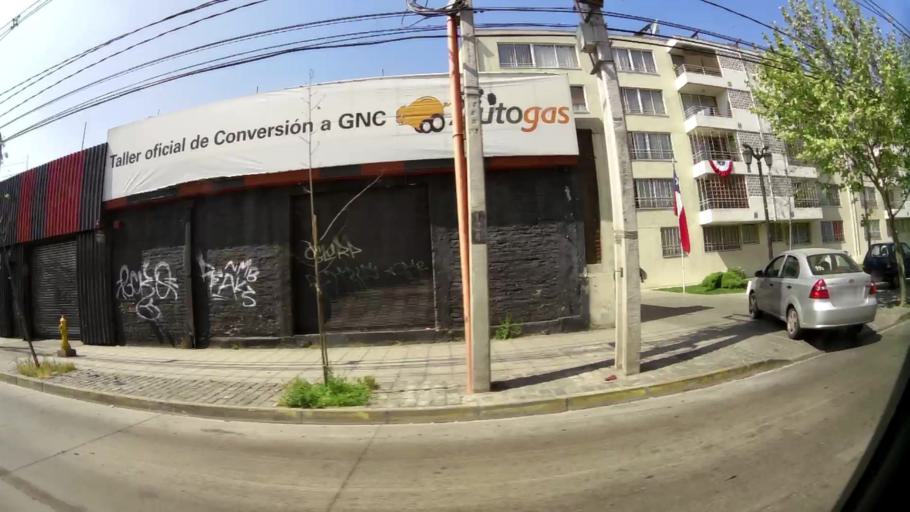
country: CL
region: Santiago Metropolitan
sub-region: Provincia de Santiago
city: Santiago
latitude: -33.4670
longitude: -70.6791
